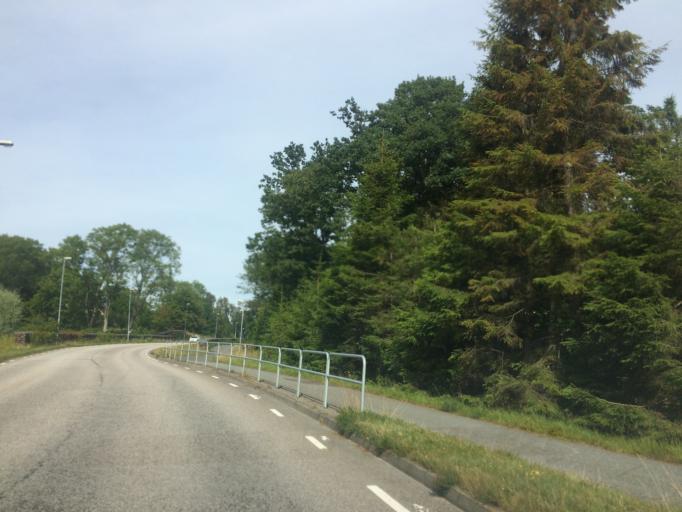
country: SE
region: Vaestra Goetaland
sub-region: Partille Kommun
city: Ojersjo
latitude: 57.6910
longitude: 12.1182
